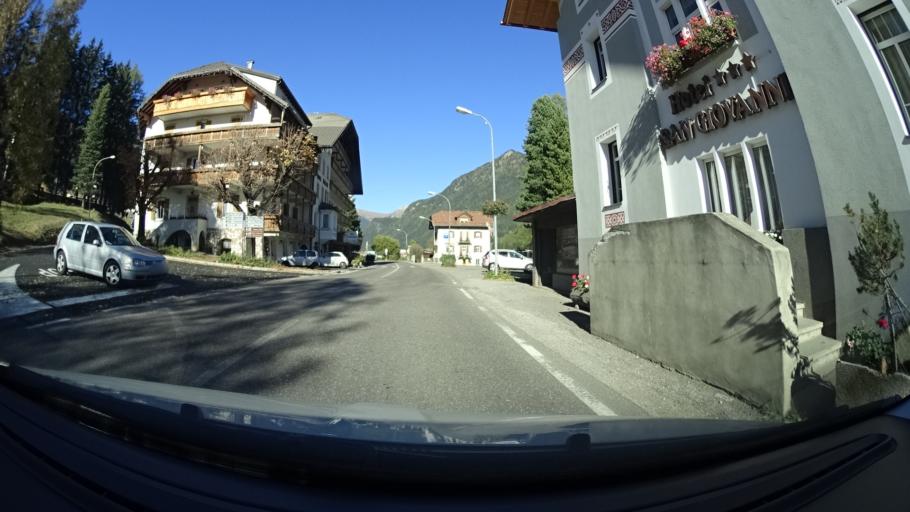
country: IT
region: Trentino-Alto Adige
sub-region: Provincia di Trento
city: Vigo di Fassa
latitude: 46.4205
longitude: 11.6815
